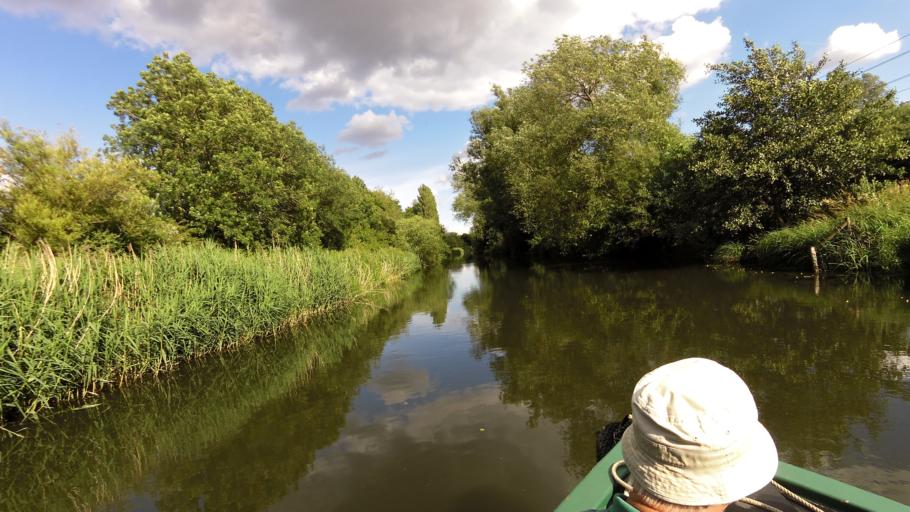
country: GB
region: England
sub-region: West Berkshire
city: Thatcham
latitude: 51.3947
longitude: -1.2793
